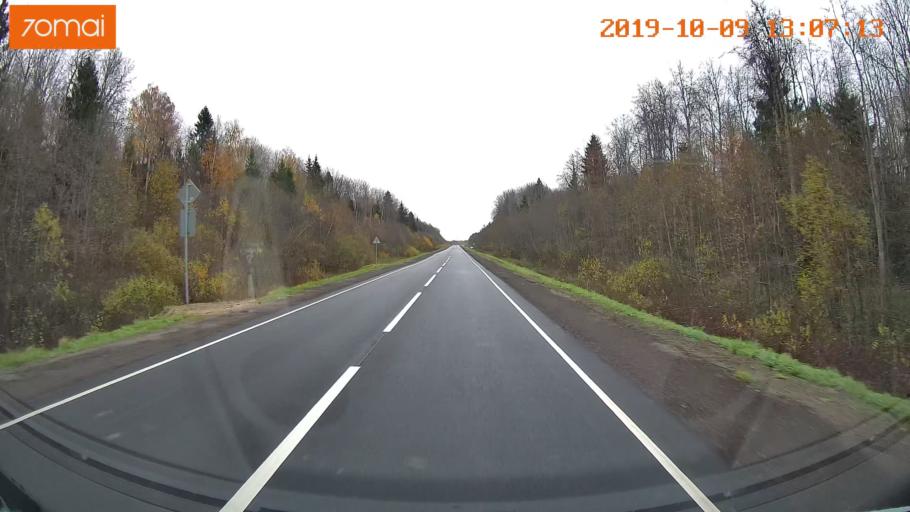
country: RU
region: Jaroslavl
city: Lyubim
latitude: 58.3559
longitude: 40.6352
